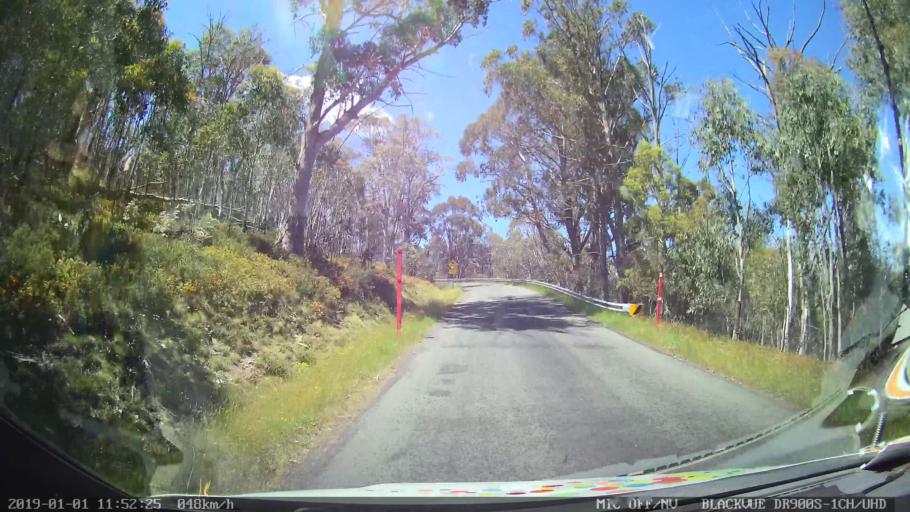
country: AU
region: New South Wales
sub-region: Snowy River
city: Jindabyne
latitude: -35.8889
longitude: 148.4346
